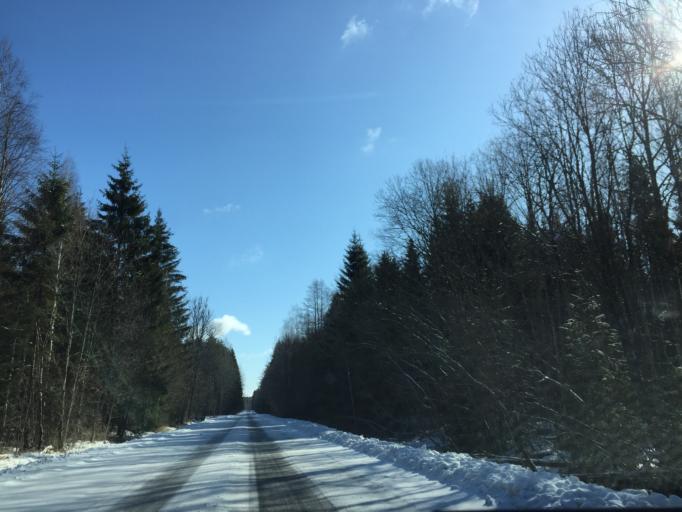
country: LV
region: Salacgrivas
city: Ainazi
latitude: 57.9973
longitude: 24.5455
